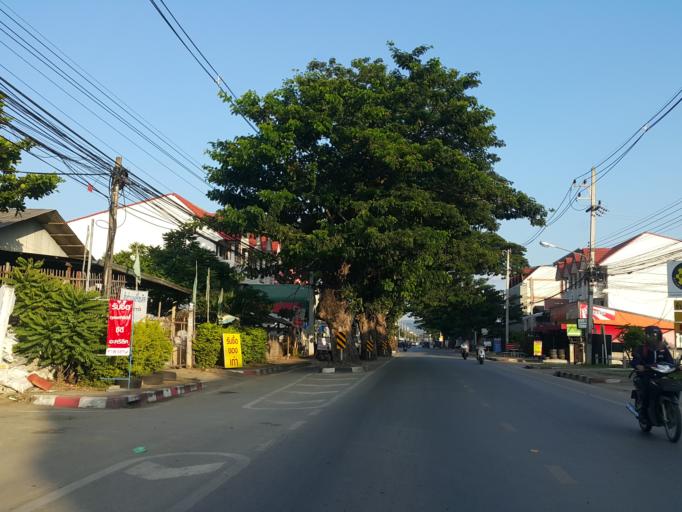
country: TH
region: Chiang Mai
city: San Kamphaeng
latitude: 18.7489
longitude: 99.1124
